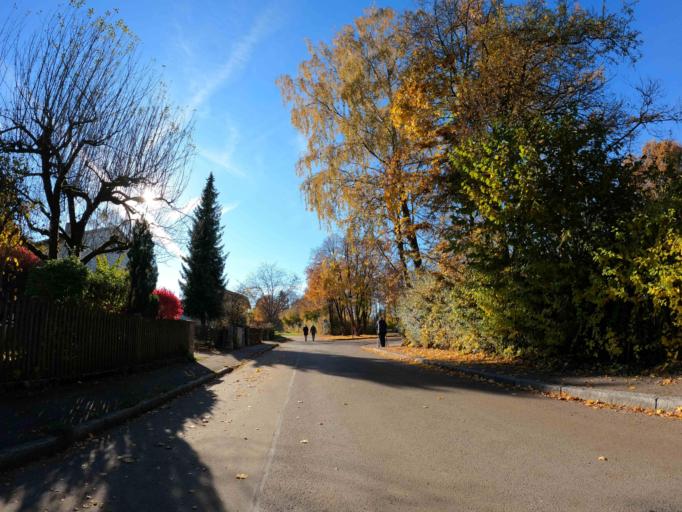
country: DE
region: Bavaria
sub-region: Upper Bavaria
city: Oberhaching
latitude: 48.0272
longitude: 11.6017
